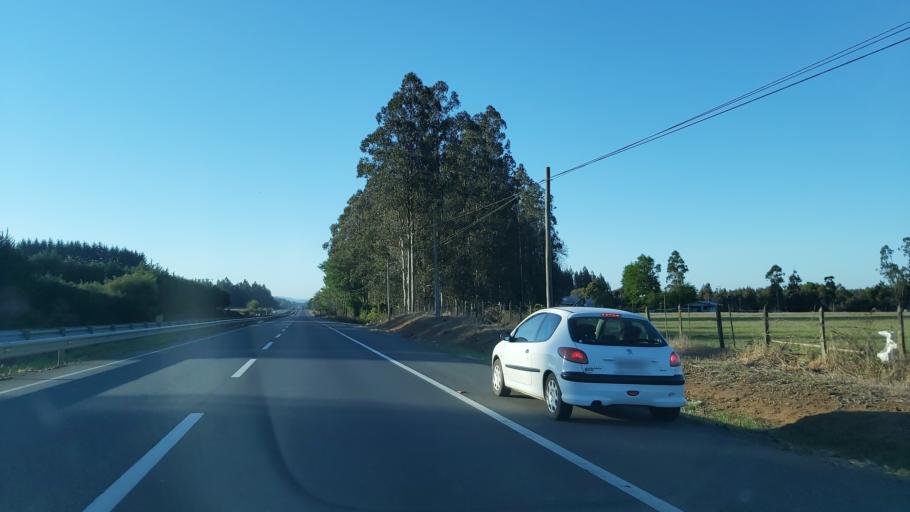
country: CL
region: Araucania
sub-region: Provincia de Malleco
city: Victoria
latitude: -38.1125
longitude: -72.3407
